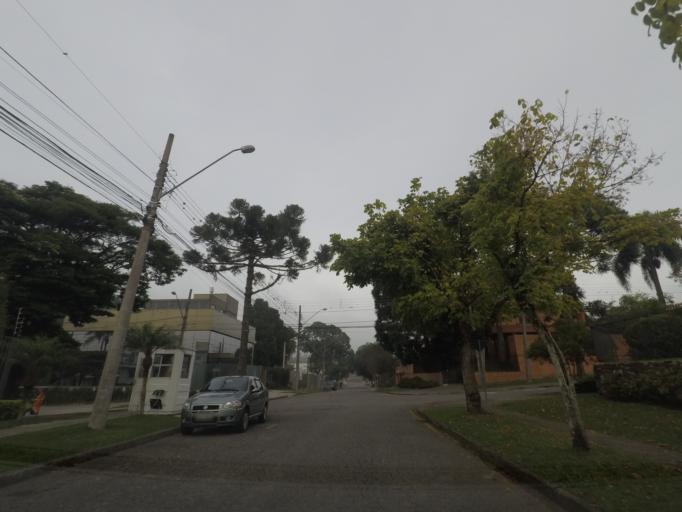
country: BR
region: Parana
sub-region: Curitiba
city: Curitiba
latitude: -25.4413
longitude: -49.2914
